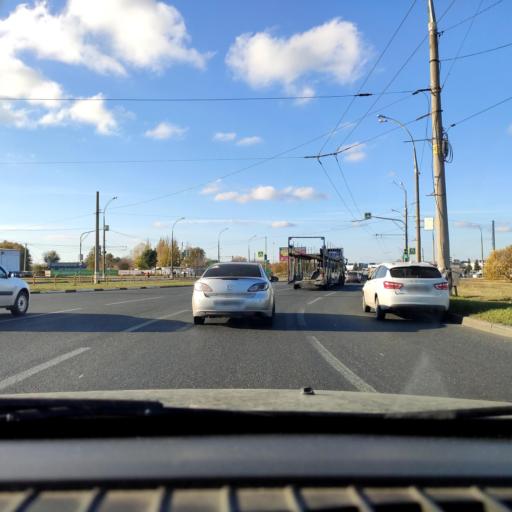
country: RU
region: Samara
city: Tol'yatti
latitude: 53.5527
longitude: 49.2623
